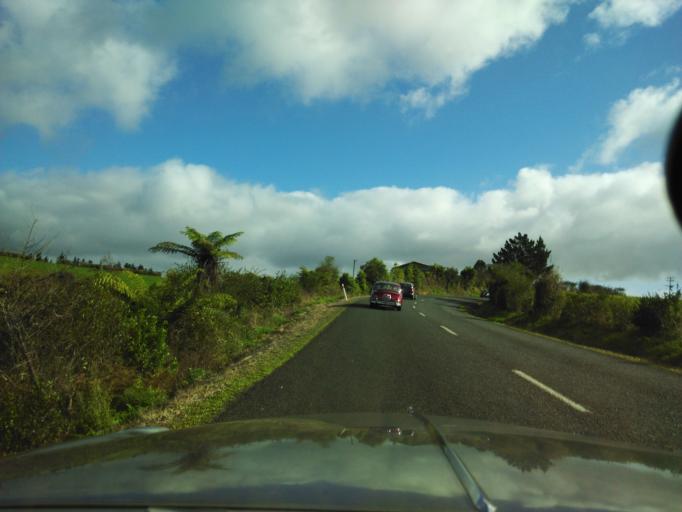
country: NZ
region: Auckland
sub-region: Auckland
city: Red Hill
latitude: -37.0726
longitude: 175.0726
